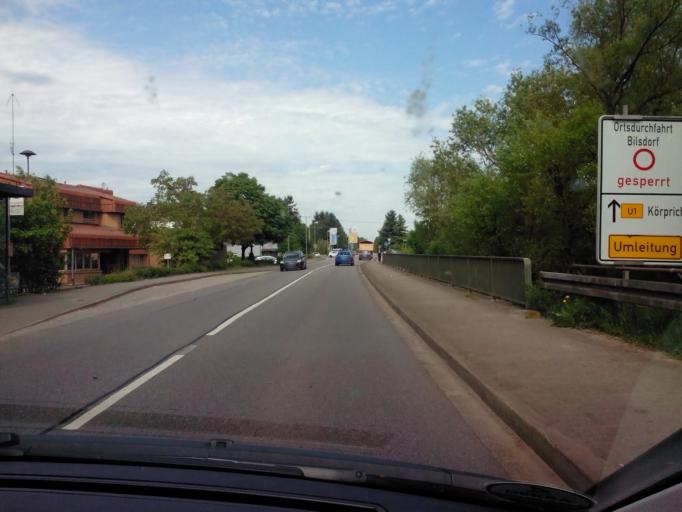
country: DE
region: Saarland
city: Nalbach
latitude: 49.3770
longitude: 6.7885
